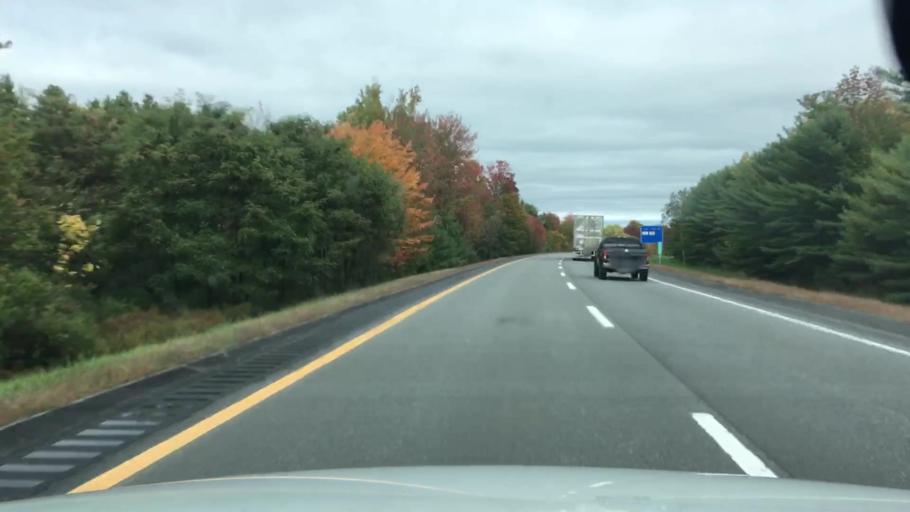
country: US
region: Maine
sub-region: Penobscot County
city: Newport
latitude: 44.8350
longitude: -69.3088
